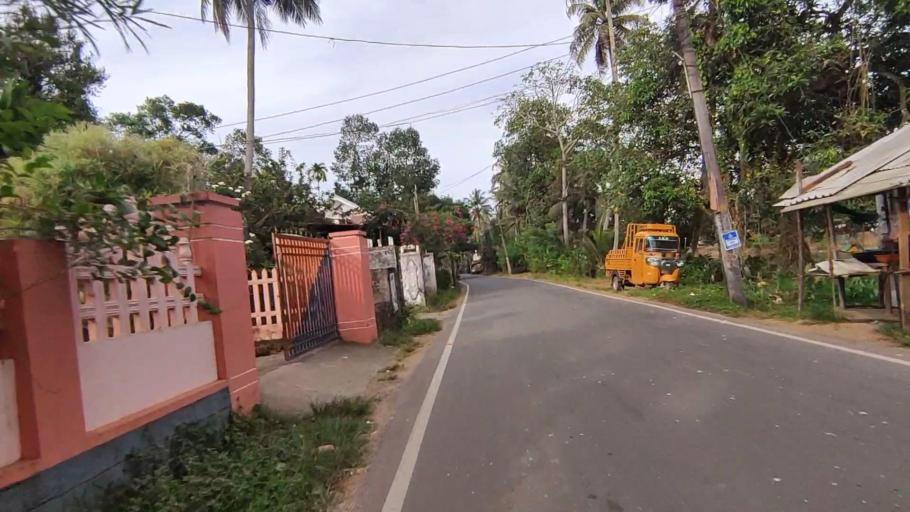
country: IN
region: Kerala
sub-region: Kottayam
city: Kottayam
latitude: 9.5917
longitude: 76.4994
